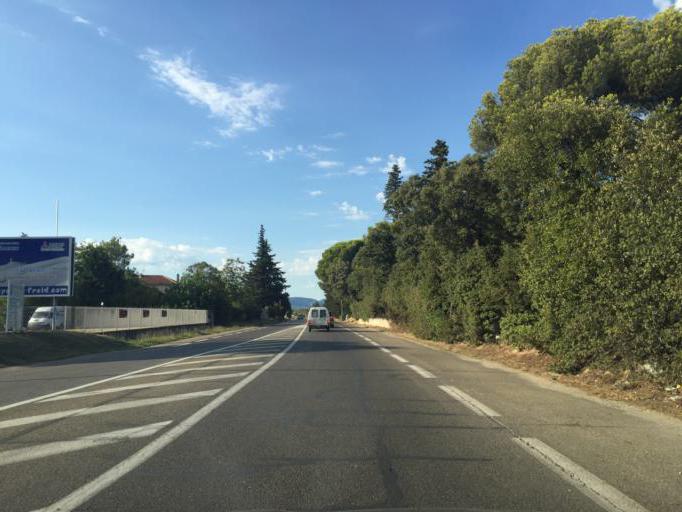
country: FR
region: Provence-Alpes-Cote d'Azur
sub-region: Departement du Vaucluse
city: Carpentras
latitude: 44.0265
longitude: 5.0523
